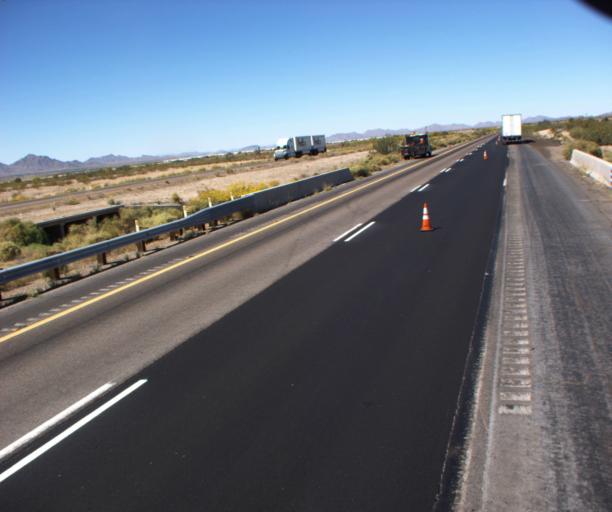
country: US
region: Arizona
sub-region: Maricopa County
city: Gila Bend
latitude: 33.0526
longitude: -112.6436
